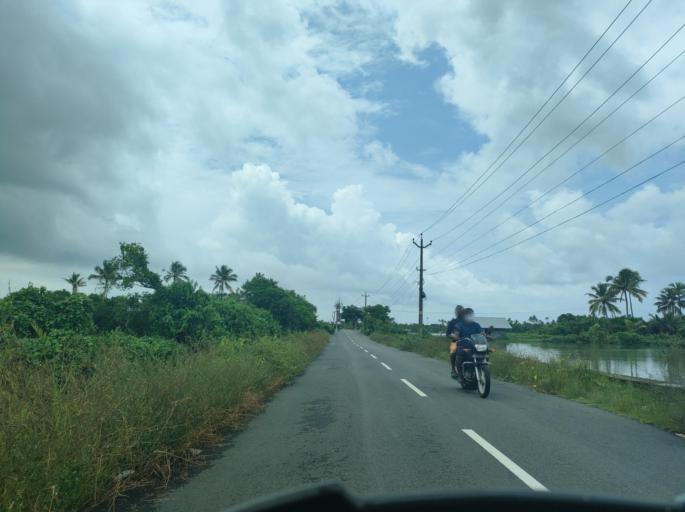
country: IN
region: Kerala
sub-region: Ernakulam
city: Elur
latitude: 10.0549
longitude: 76.2082
